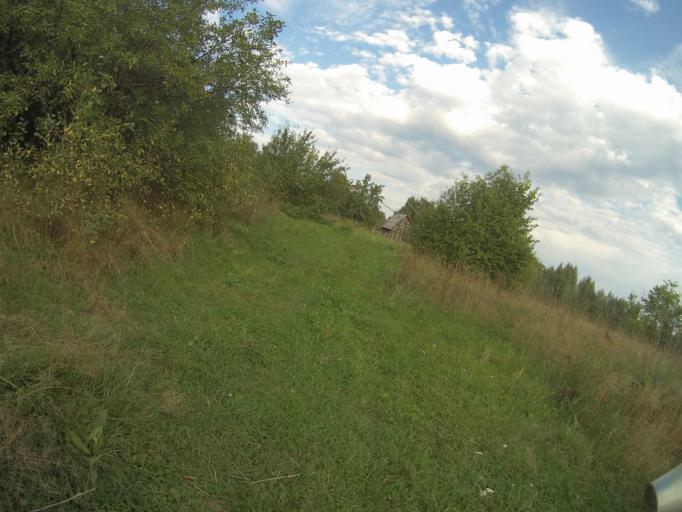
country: RU
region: Vladimir
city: Vorsha
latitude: 55.9806
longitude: 40.1722
